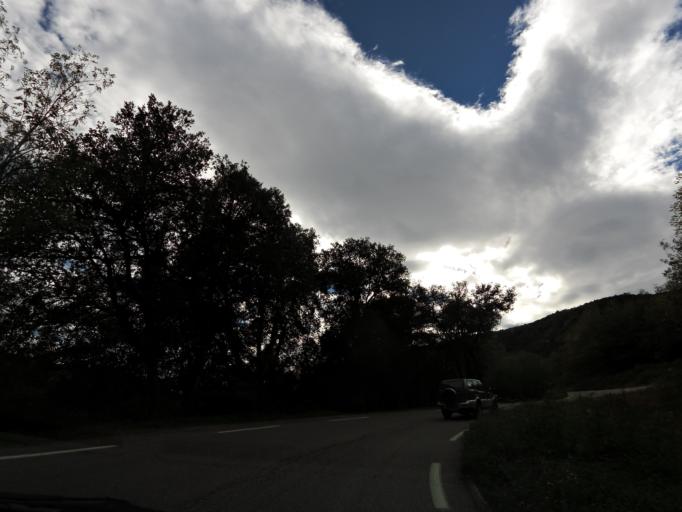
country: FR
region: Languedoc-Roussillon
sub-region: Departement du Gard
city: Lasalle
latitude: 44.0139
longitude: 3.8493
